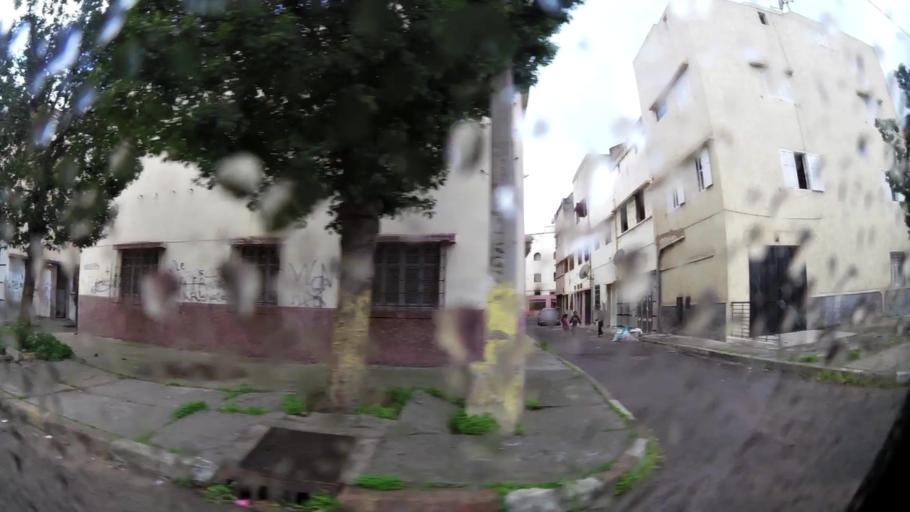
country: MA
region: Grand Casablanca
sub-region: Mohammedia
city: Mohammedia
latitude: 33.6828
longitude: -7.3901
